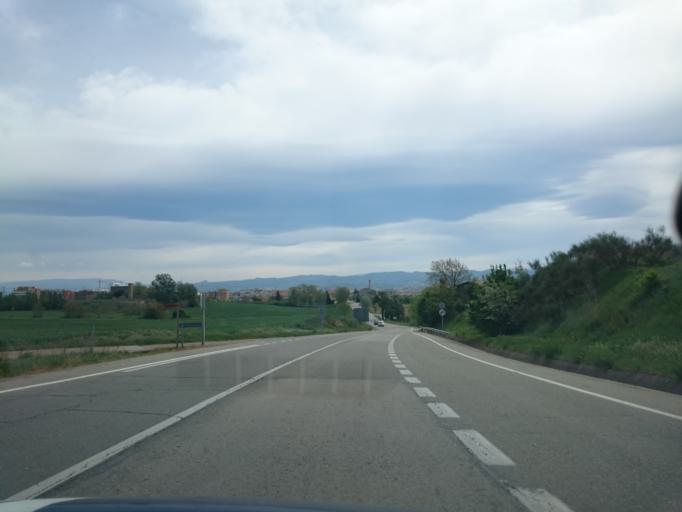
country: ES
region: Catalonia
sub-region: Provincia de Barcelona
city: Vic
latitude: 41.9273
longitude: 2.2328
